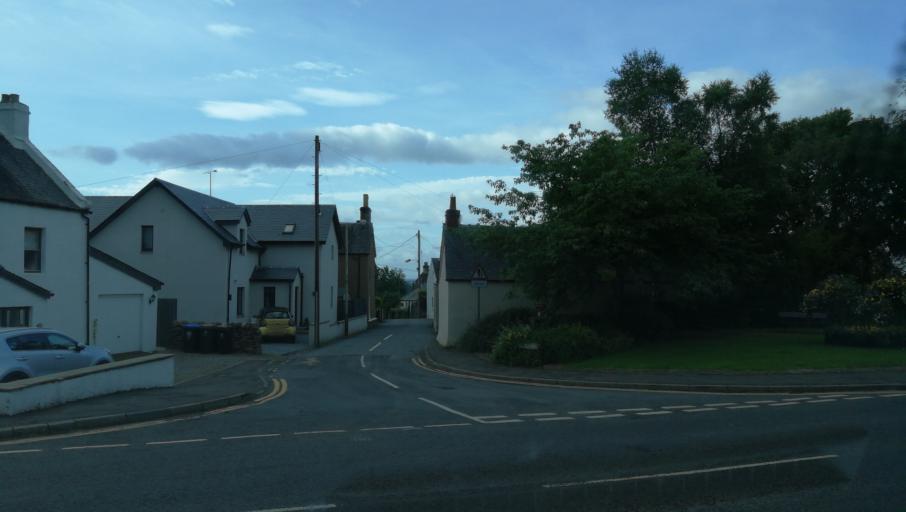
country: GB
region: Scotland
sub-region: Perth and Kinross
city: Blairgowrie
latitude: 56.5966
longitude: -3.3218
